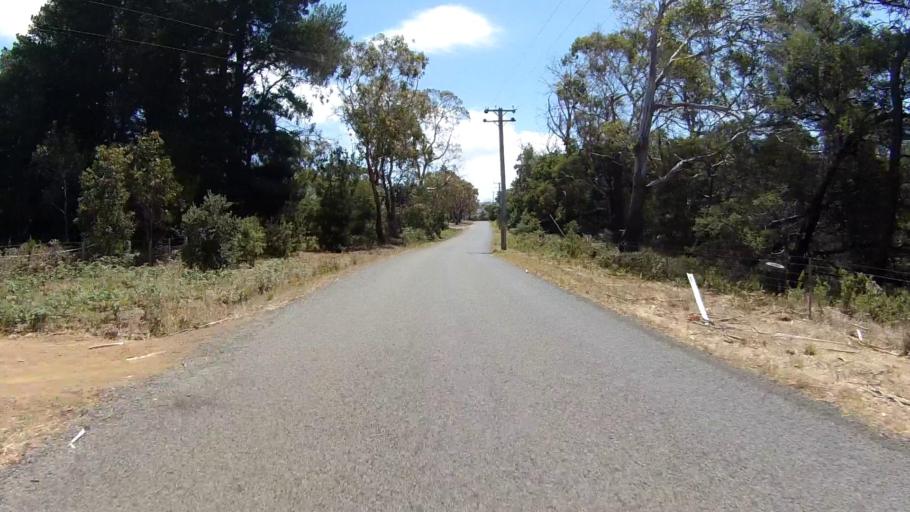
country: AU
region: Tasmania
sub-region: Clarence
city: Sandford
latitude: -42.9334
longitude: 147.5004
